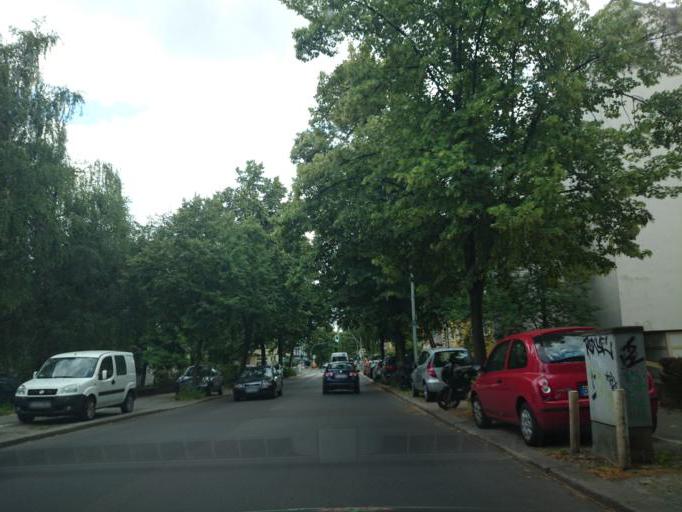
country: DE
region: Berlin
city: Mariendorf
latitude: 52.4479
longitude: 13.3702
